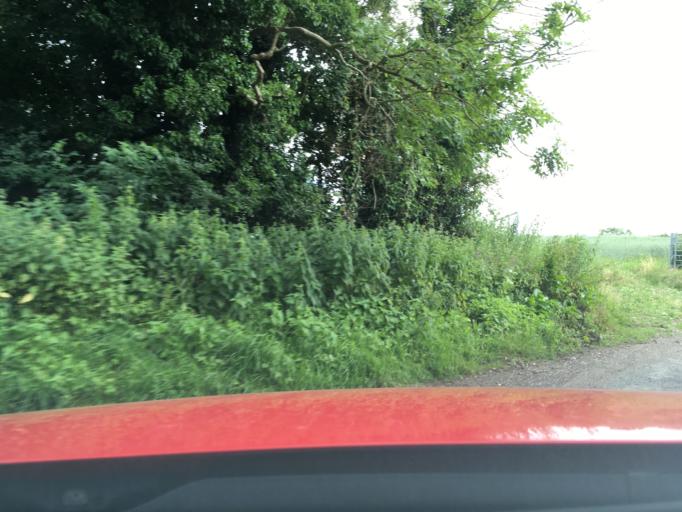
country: GB
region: England
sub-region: Gloucestershire
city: Cinderford
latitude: 51.7997
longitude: -2.4155
